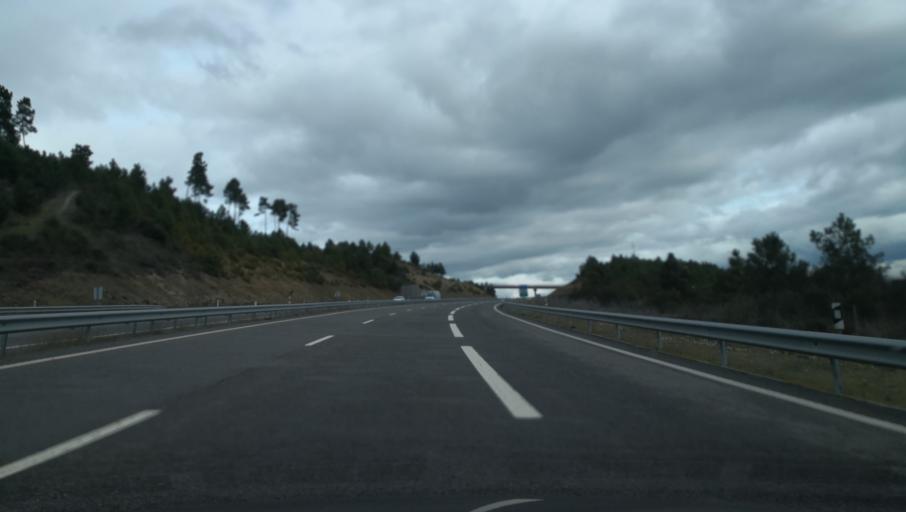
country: PT
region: Vila Real
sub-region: Boticas
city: Boticas
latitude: 41.6903
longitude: -7.5611
